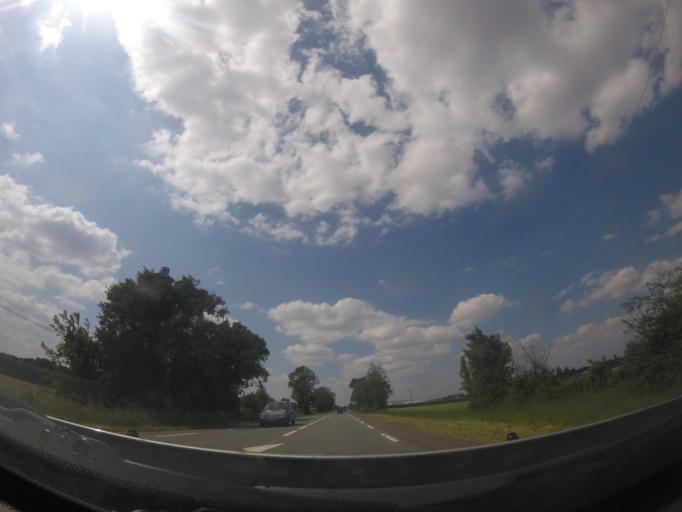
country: FR
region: Poitou-Charentes
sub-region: Departement de la Charente-Maritime
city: Saint-Porchaire
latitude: 45.8521
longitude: -0.8250
